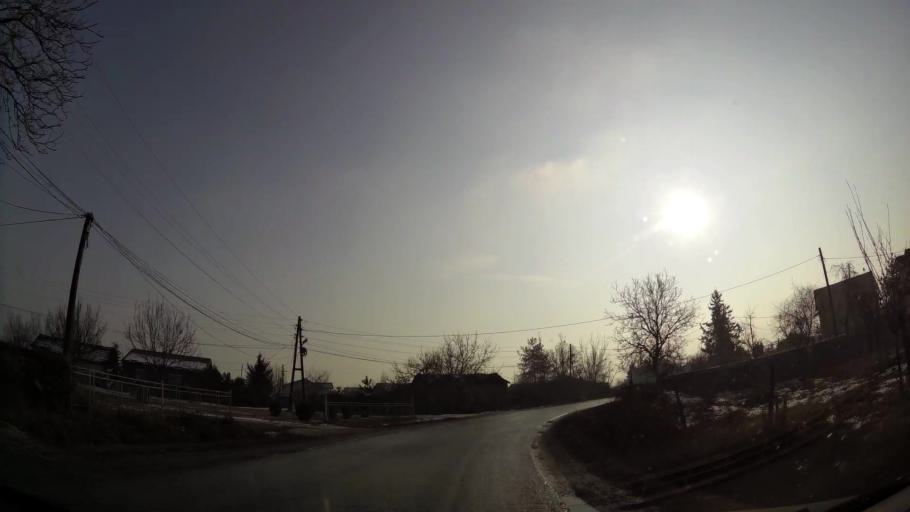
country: MK
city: Kadino
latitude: 41.9656
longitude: 21.6000
